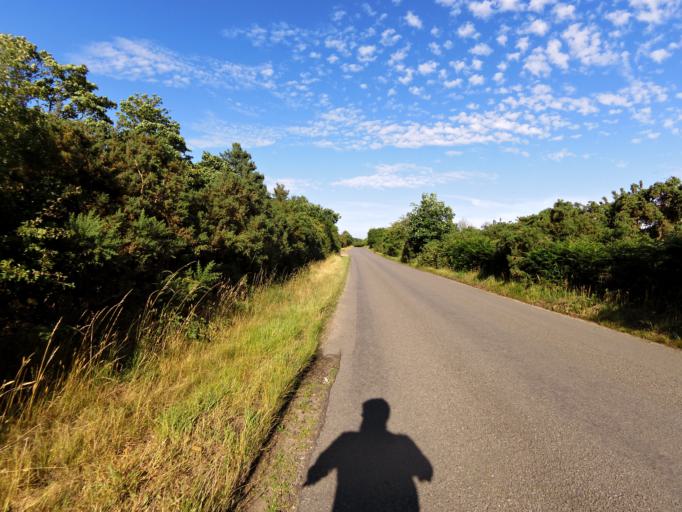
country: GB
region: England
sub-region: Suffolk
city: Leiston
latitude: 52.2694
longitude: 1.6049
